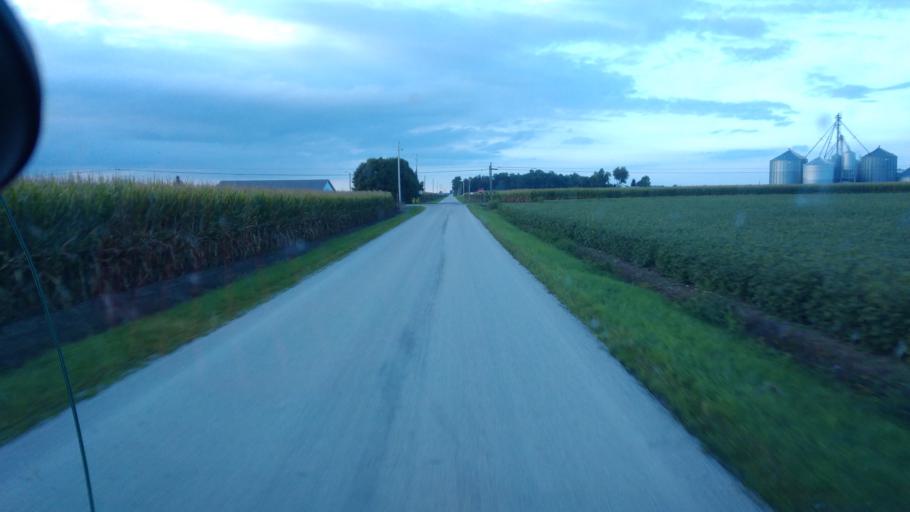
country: US
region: Ohio
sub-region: Hardin County
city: Kenton
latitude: 40.6567
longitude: -83.5149
